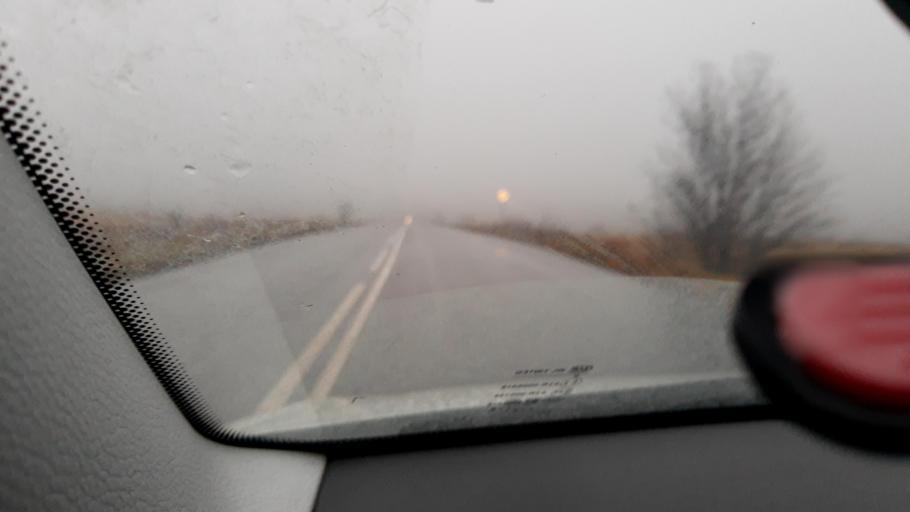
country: RU
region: Bashkortostan
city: Iglino
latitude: 54.8993
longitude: 56.2241
